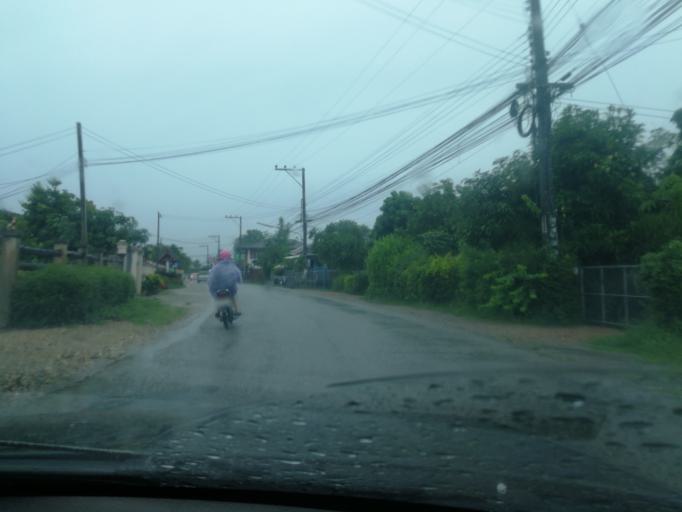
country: TH
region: Chiang Mai
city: San Pa Tong
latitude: 18.5983
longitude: 98.9103
